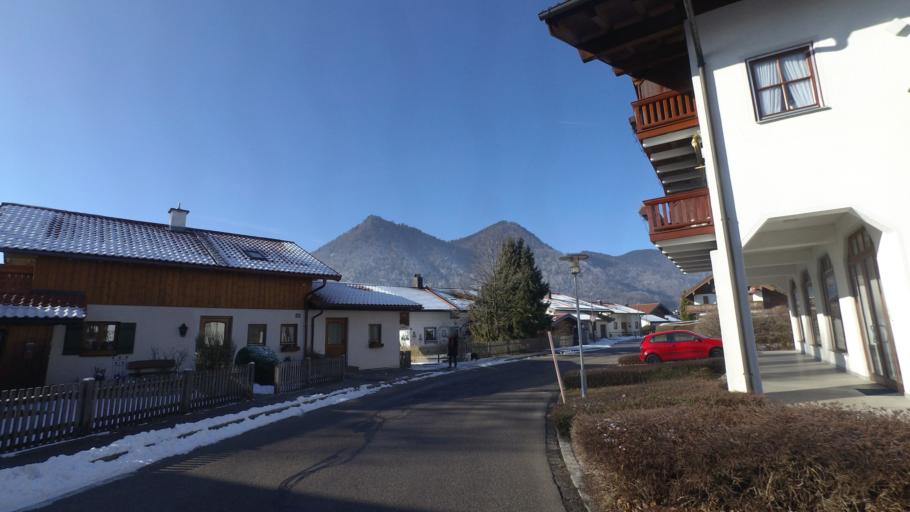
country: DE
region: Bavaria
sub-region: Upper Bavaria
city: Ruhpolding
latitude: 47.7665
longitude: 12.6501
